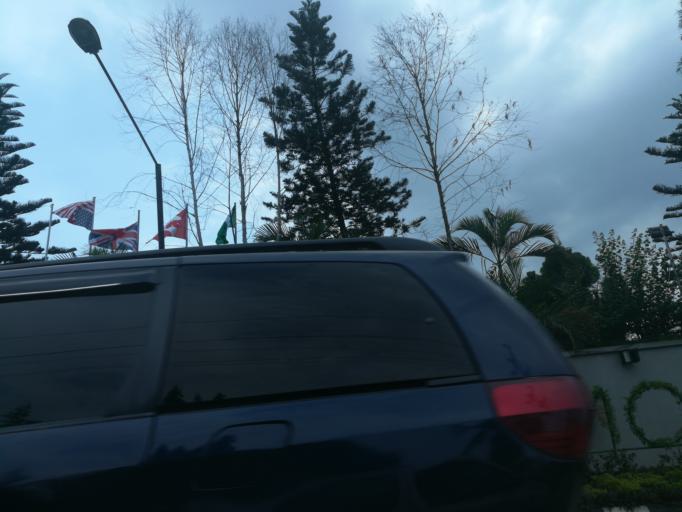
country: NG
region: Lagos
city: Ikeja
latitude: 6.6089
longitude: 3.3614
